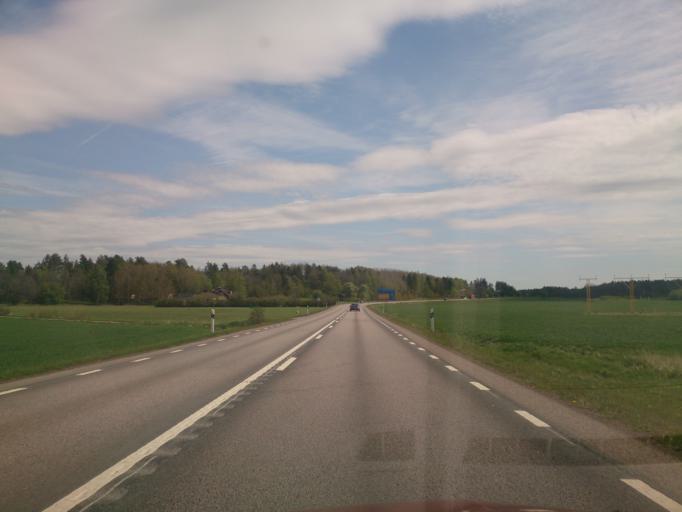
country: SE
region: OEstergoetland
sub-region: Linkopings Kommun
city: Sturefors
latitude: 58.4007
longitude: 15.7071
